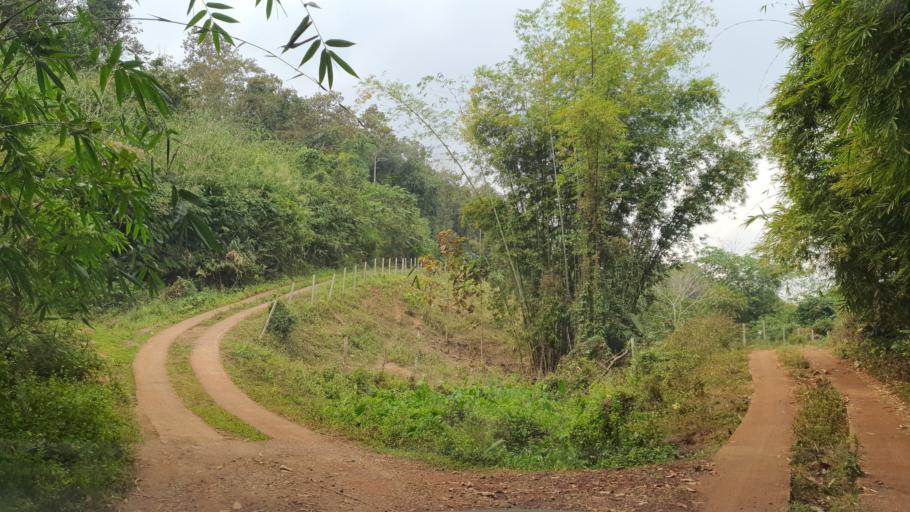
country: TH
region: Chiang Mai
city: Mae Wang
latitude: 18.6554
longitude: 98.6524
